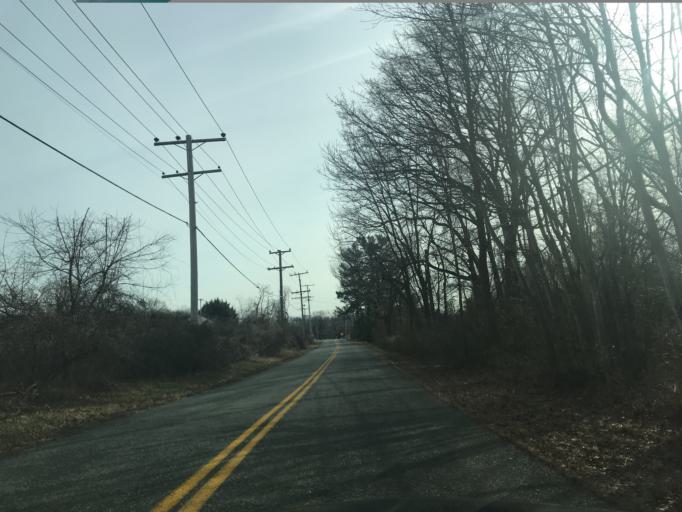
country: US
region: Maryland
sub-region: Harford County
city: Havre de Grace
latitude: 39.5741
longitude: -76.1501
